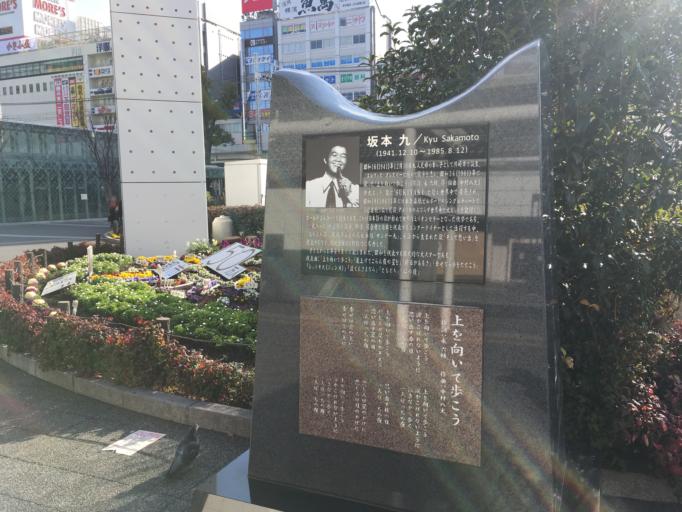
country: JP
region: Kanagawa
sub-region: Kawasaki-shi
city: Kawasaki
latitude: 35.5305
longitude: 139.6978
